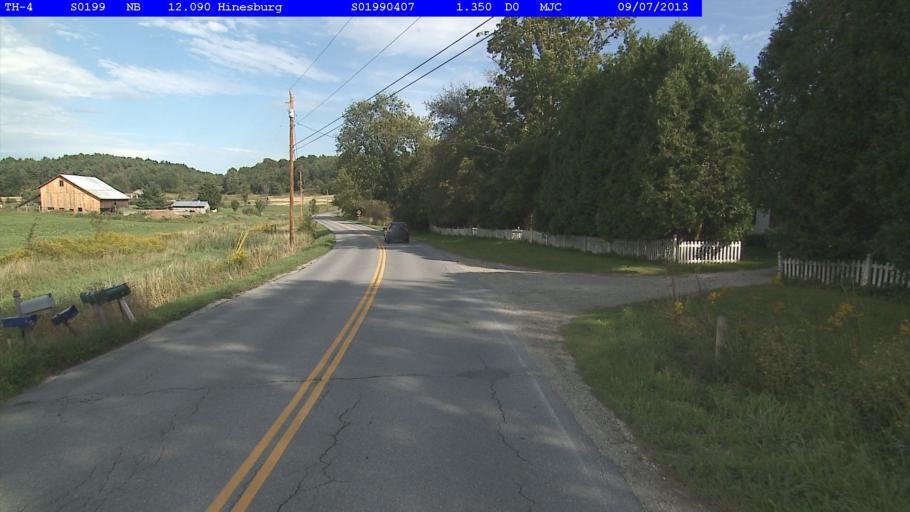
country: US
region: Vermont
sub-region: Chittenden County
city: Hinesburg
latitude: 44.2974
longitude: -73.1087
